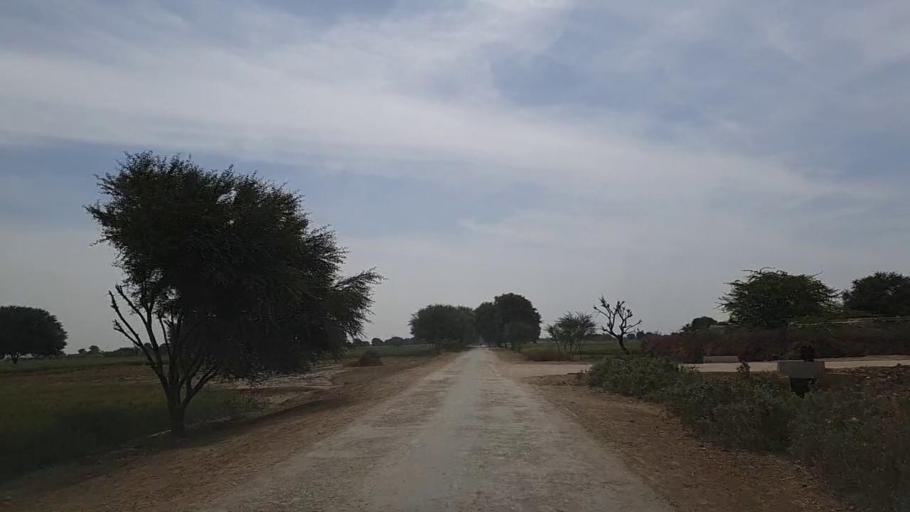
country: PK
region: Sindh
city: Samaro
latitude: 25.2882
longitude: 69.4538
